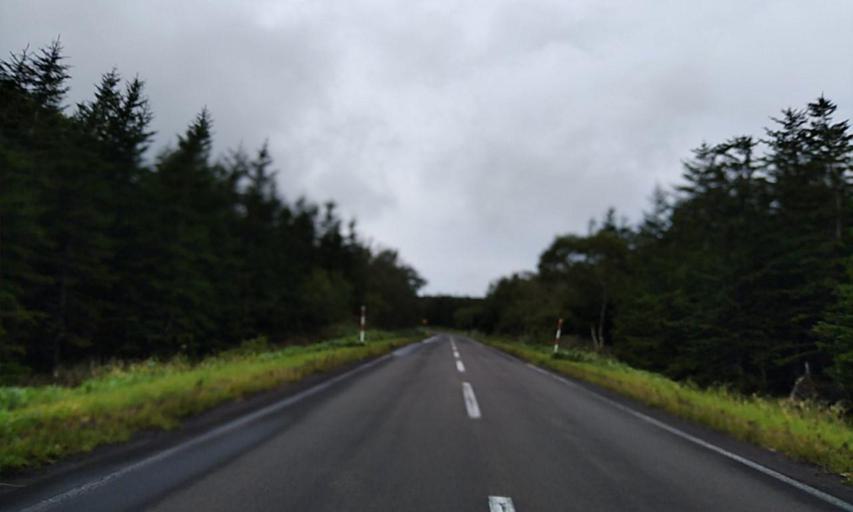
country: JP
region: Hokkaido
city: Abashiri
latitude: 43.6076
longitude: 144.5900
